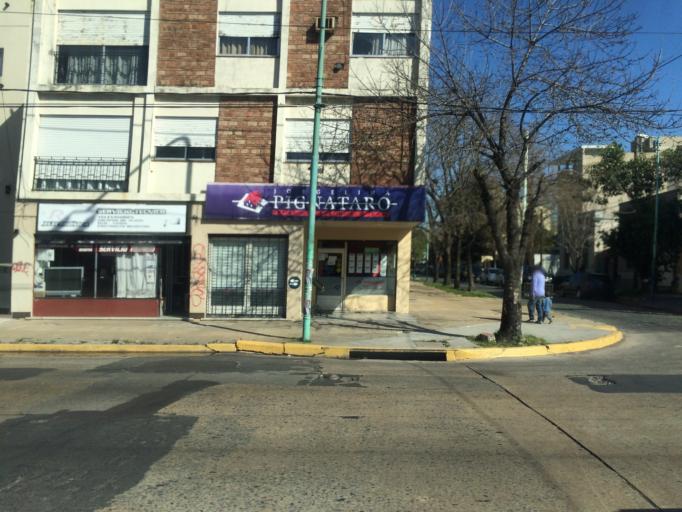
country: AR
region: Buenos Aires
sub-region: Partido de Lomas de Zamora
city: Lomas de Zamora
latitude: -34.7473
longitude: -58.3939
